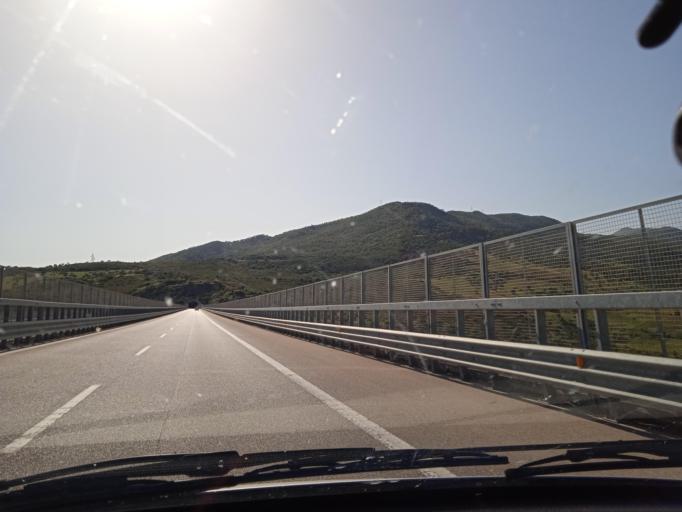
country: IT
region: Sicily
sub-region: Palermo
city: Finale
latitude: 38.0083
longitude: 14.1767
